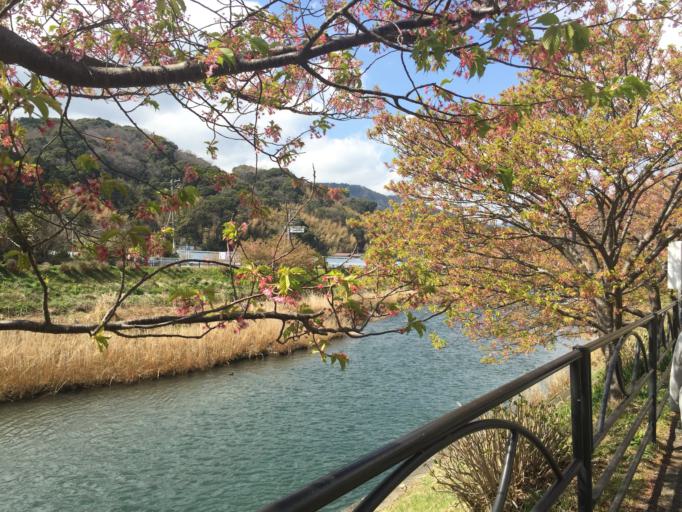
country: JP
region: Shizuoka
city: Shimoda
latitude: 34.7500
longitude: 138.9895
